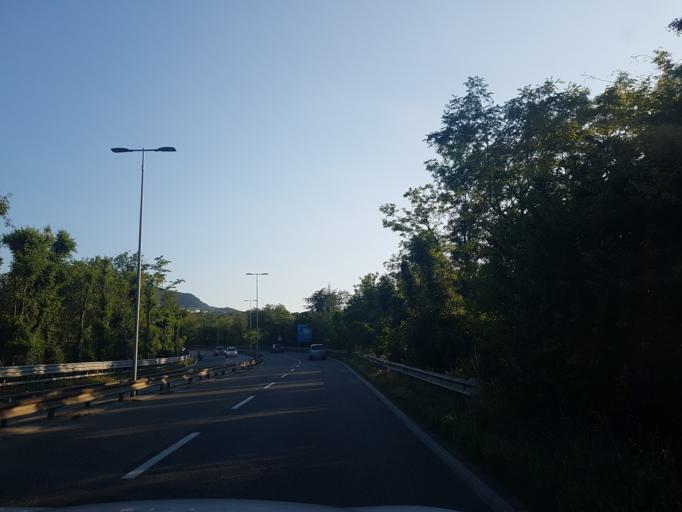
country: SM
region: Serravalle
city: Serravalle
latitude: 43.9655
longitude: 12.4719
